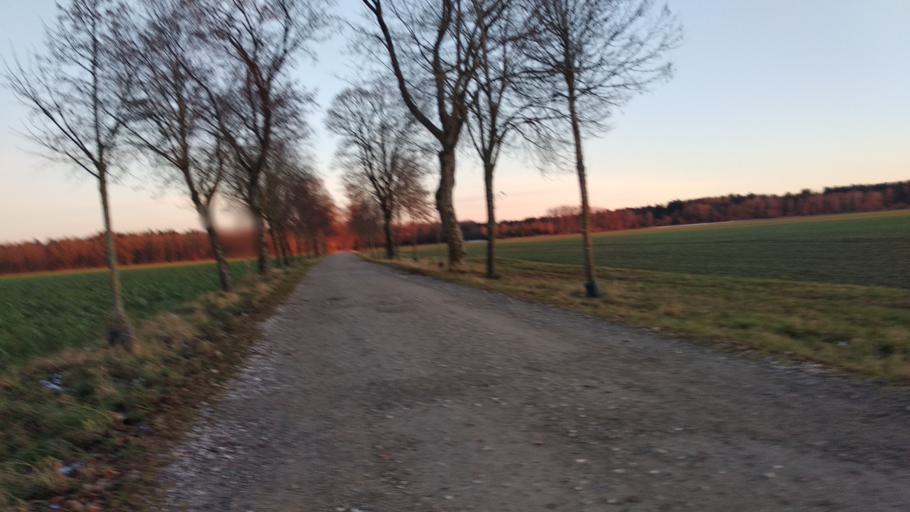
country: DE
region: Bavaria
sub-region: Upper Bavaria
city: Vaterstetten
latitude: 48.0712
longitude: 11.7788
